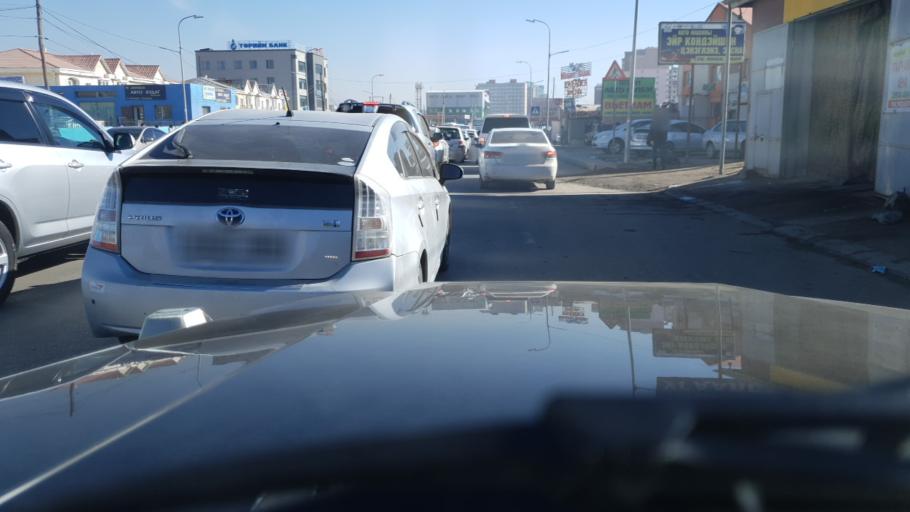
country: MN
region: Ulaanbaatar
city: Ulaanbaatar
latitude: 47.9241
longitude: 106.9697
